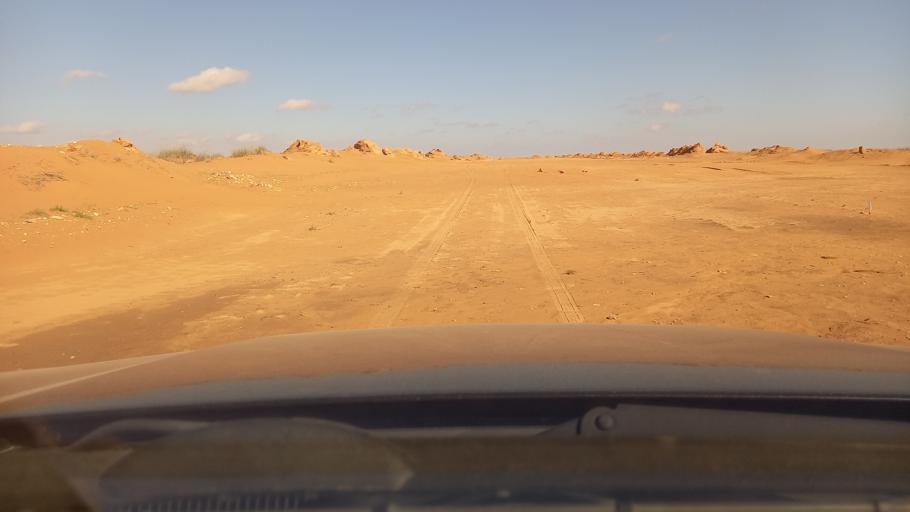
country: TN
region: Madanin
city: Medenine
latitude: 33.2346
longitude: 10.5500
